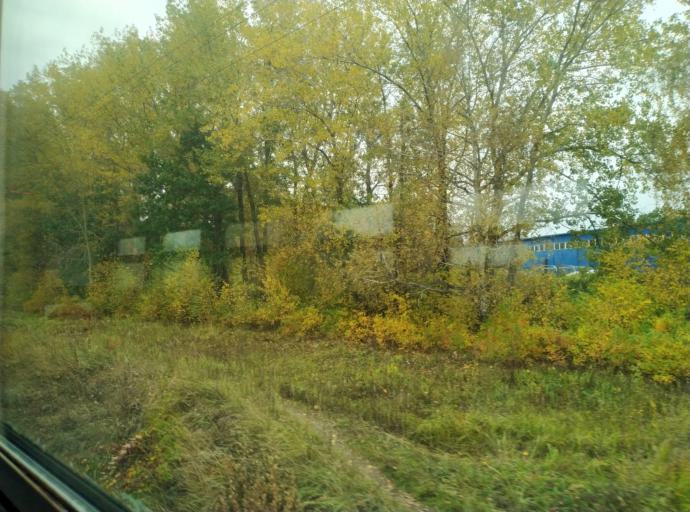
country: RU
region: Moskovskaya
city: Bol'shiye Vyazemy
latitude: 55.6180
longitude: 36.9725
